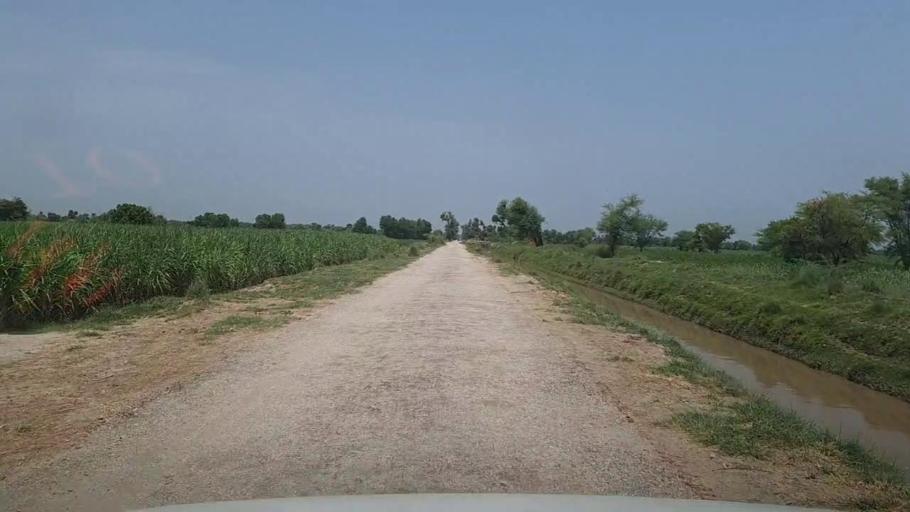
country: PK
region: Sindh
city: Karaundi
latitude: 26.8879
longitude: 68.3337
